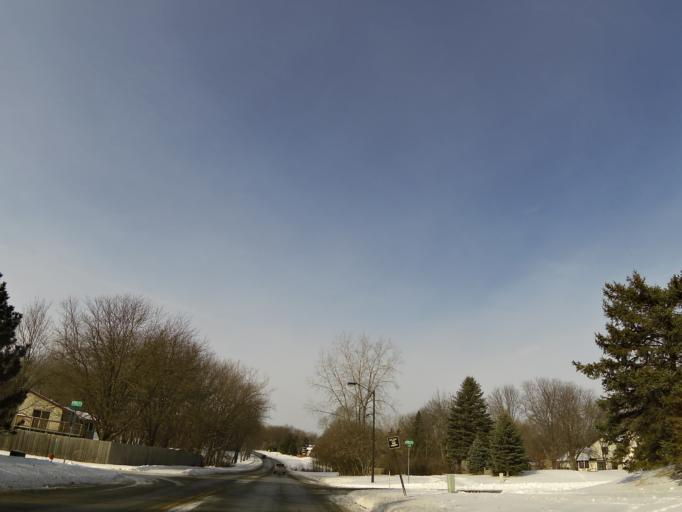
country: US
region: Minnesota
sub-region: Hennepin County
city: Eden Prairie
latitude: 44.8429
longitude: -93.4317
